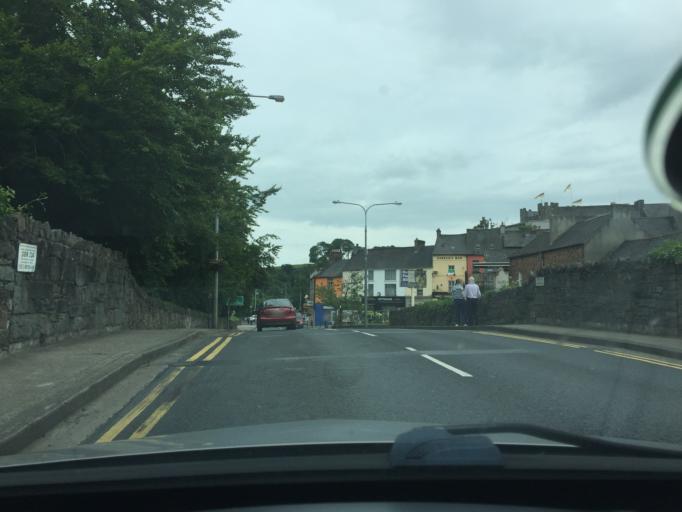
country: IE
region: Leinster
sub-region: Loch Garman
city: Enniscorthy
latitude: 52.5027
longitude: -6.5679
